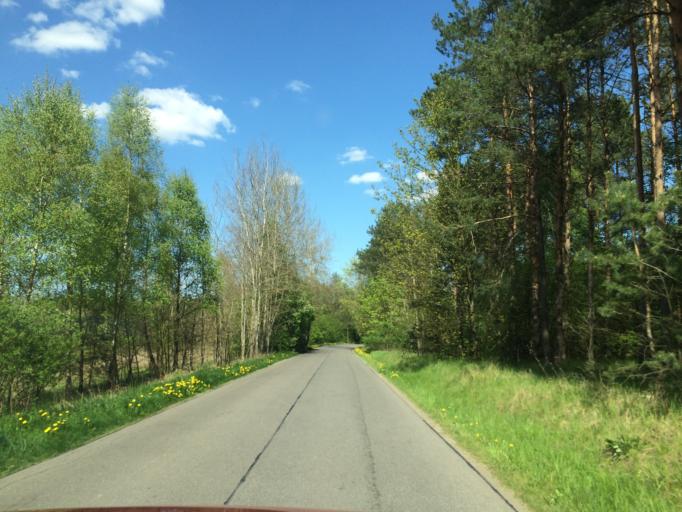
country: PL
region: Warmian-Masurian Voivodeship
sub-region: Powiat ilawski
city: Lubawa
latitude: 53.3949
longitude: 19.7381
